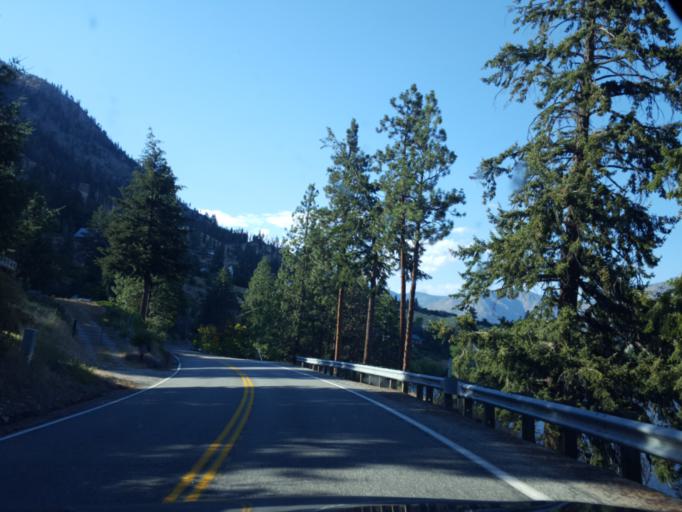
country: US
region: Washington
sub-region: Chelan County
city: Granite Falls
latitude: 47.9415
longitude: -120.2115
